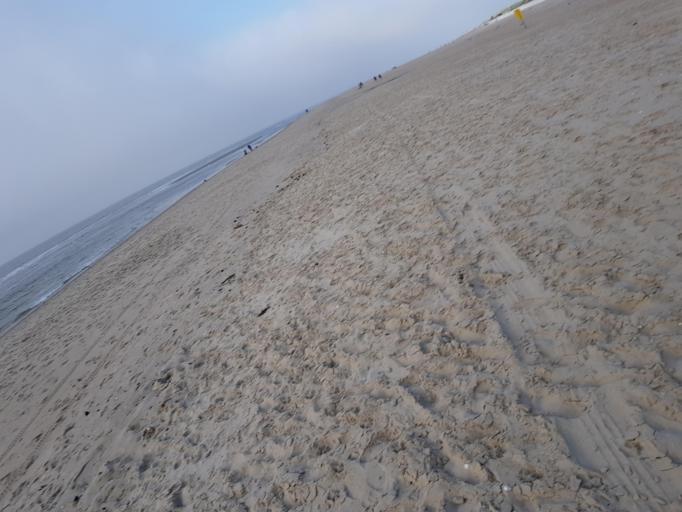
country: NL
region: North Holland
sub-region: Gemeente Texel
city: Den Burg
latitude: 53.1594
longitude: 4.8160
